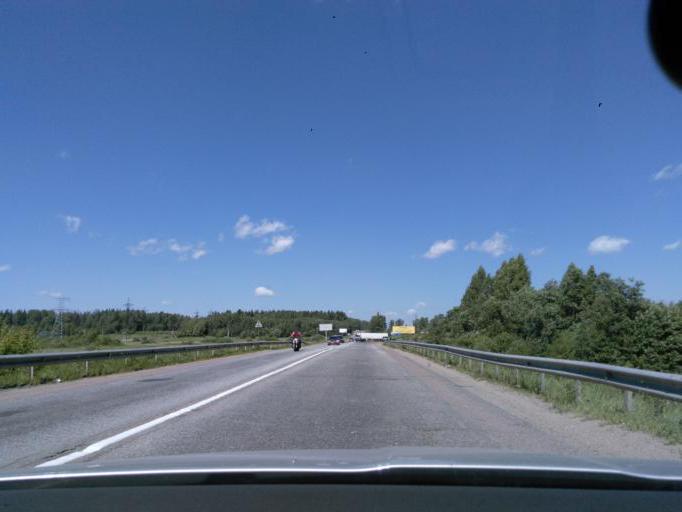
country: RU
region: Moskovskaya
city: Solnechnogorsk
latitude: 56.1519
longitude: 36.9190
